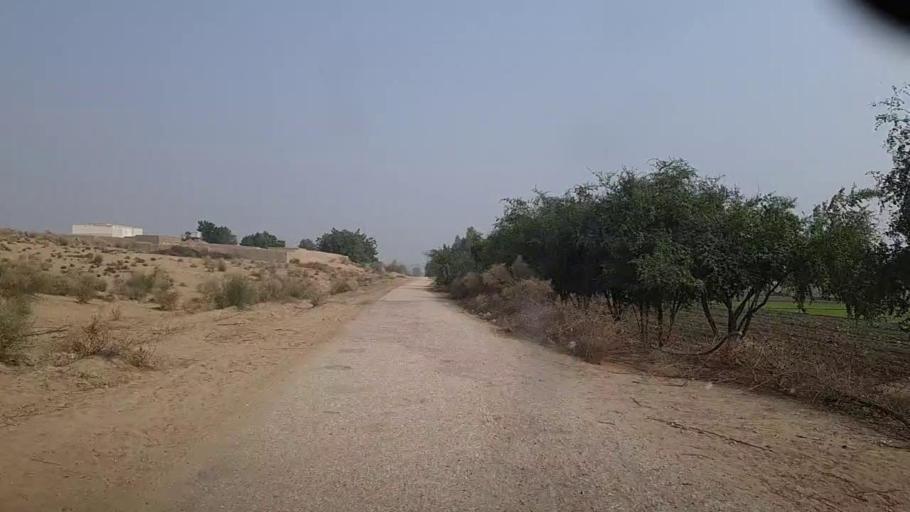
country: PK
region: Sindh
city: Bozdar
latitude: 27.0573
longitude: 68.6586
